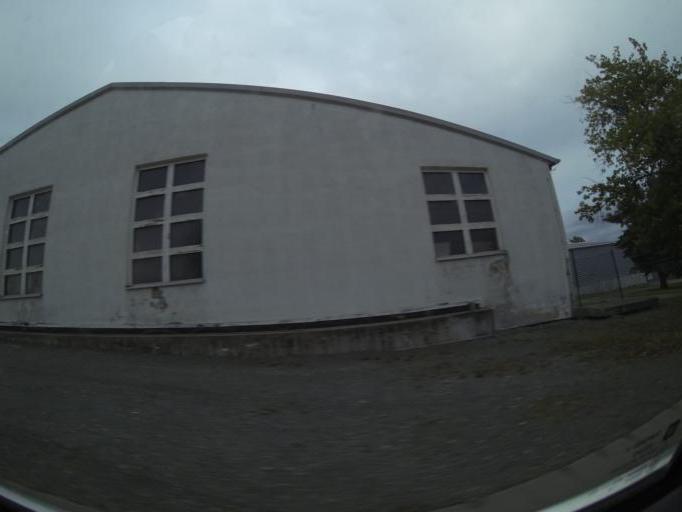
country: DE
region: Thuringia
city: Nobdenitz
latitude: 50.8799
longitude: 12.2798
